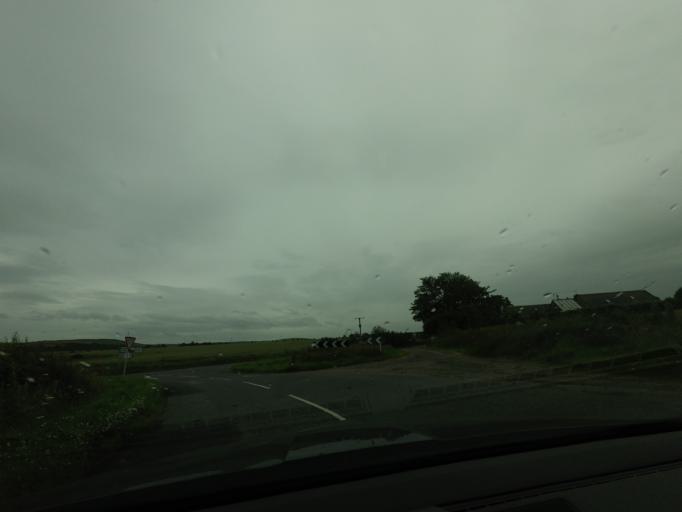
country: GB
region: Scotland
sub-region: Aberdeenshire
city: Portsoy
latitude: 57.6418
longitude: -2.6507
